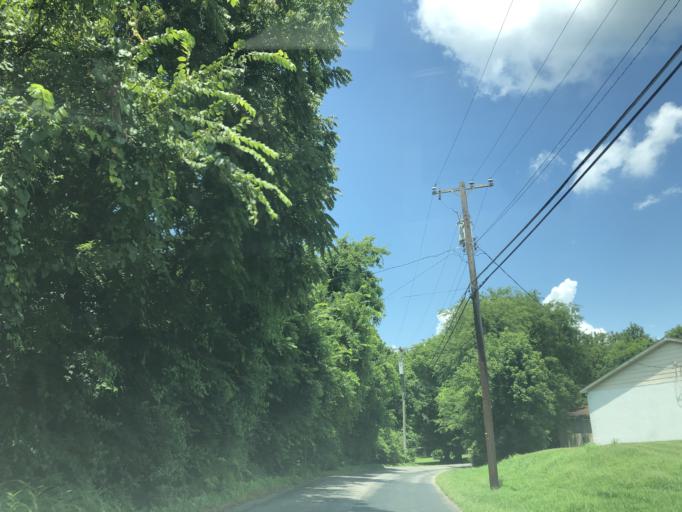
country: US
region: Tennessee
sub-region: Davidson County
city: Lakewood
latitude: 36.2013
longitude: -86.6194
